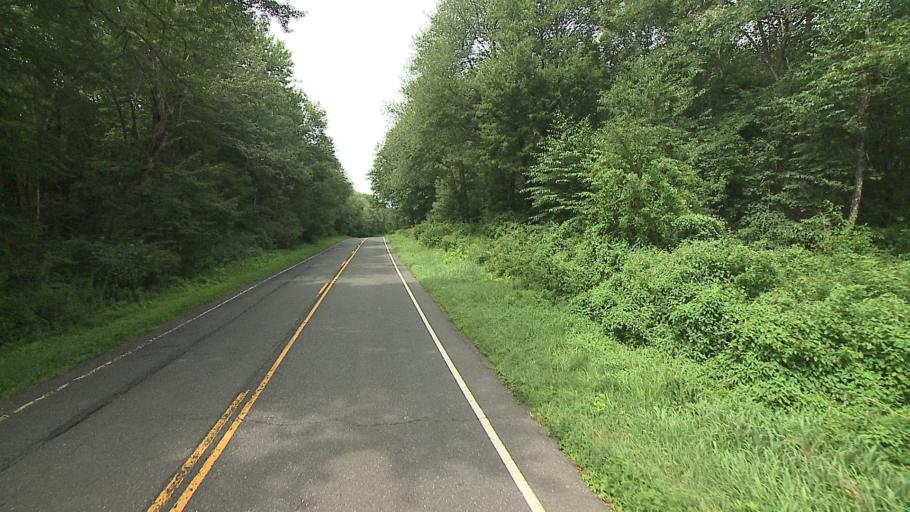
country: US
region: Connecticut
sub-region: Litchfield County
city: Woodbury
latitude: 41.5568
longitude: -73.2651
